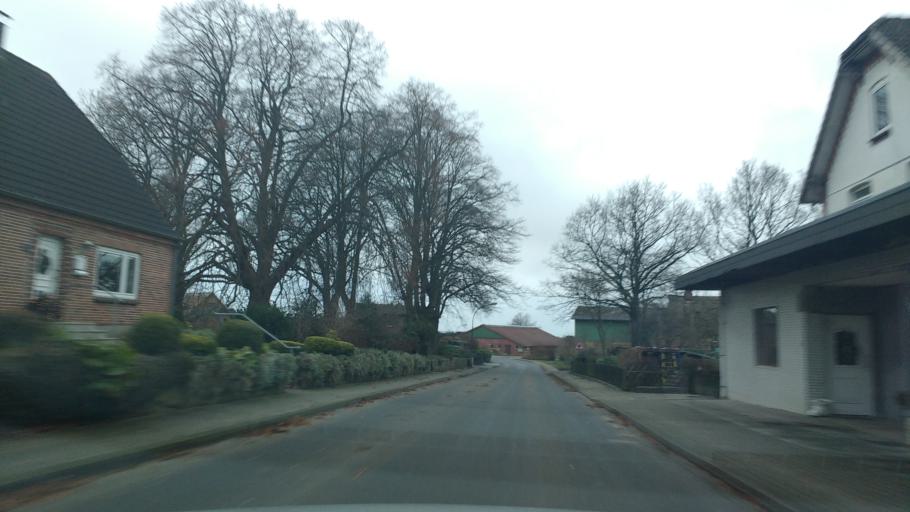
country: DE
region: Schleswig-Holstein
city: Nindorf
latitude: 54.1322
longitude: 9.6978
